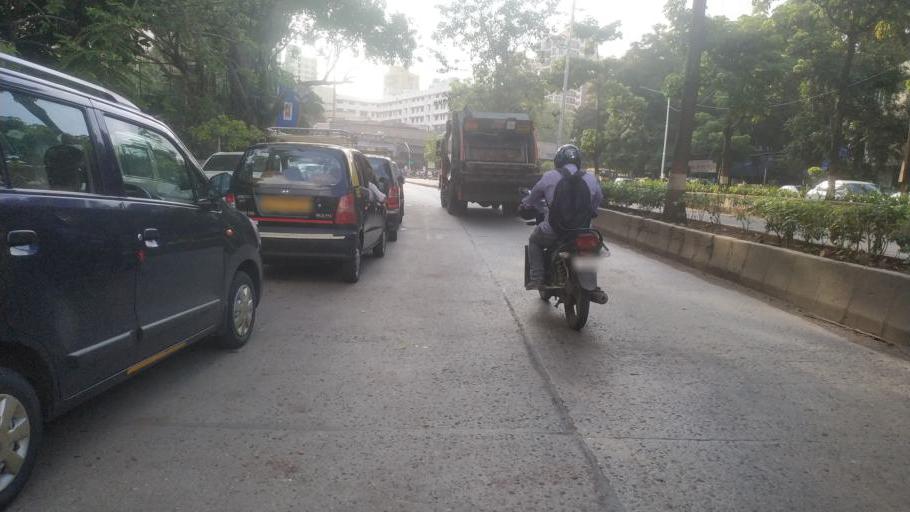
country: IN
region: Maharashtra
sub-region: Mumbai Suburban
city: Mumbai
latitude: 19.0285
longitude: 72.8586
